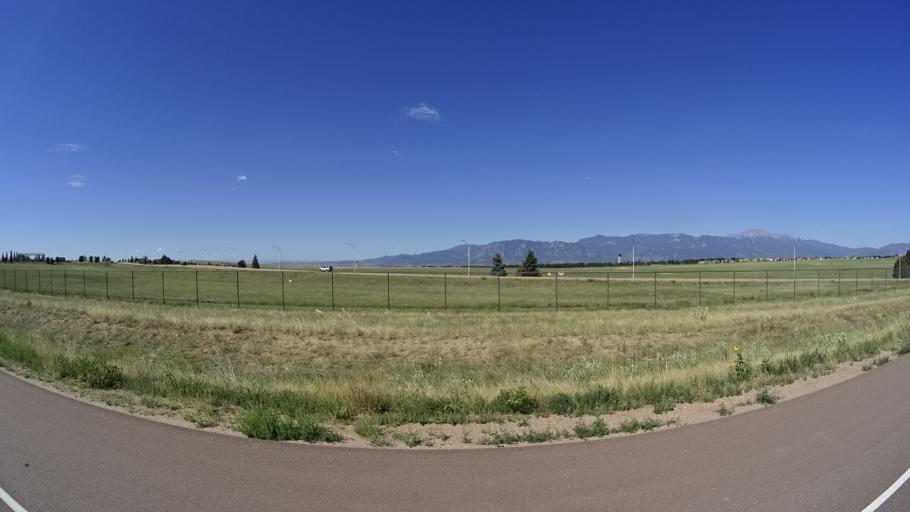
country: US
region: Colorado
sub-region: El Paso County
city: Cimarron Hills
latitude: 38.8205
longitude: -104.6794
